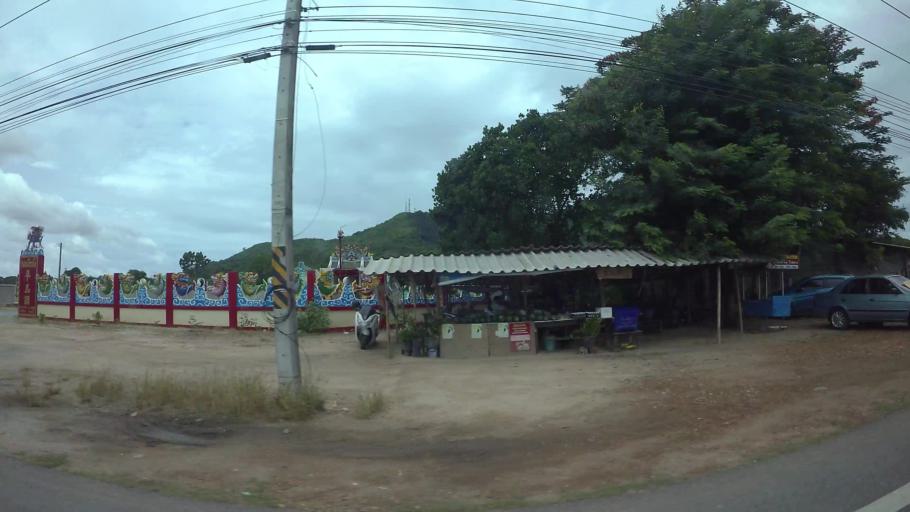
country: TH
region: Chon Buri
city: Si Racha
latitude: 13.1951
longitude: 100.9614
